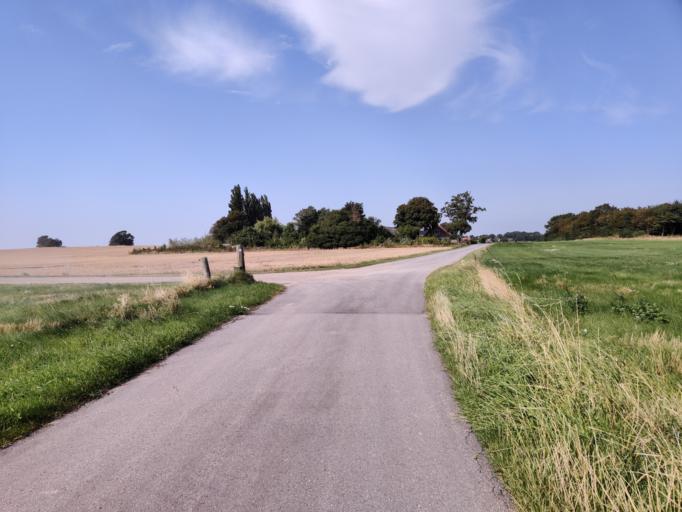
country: DK
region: Zealand
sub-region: Guldborgsund Kommune
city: Nykobing Falster
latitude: 54.6877
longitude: 11.8998
